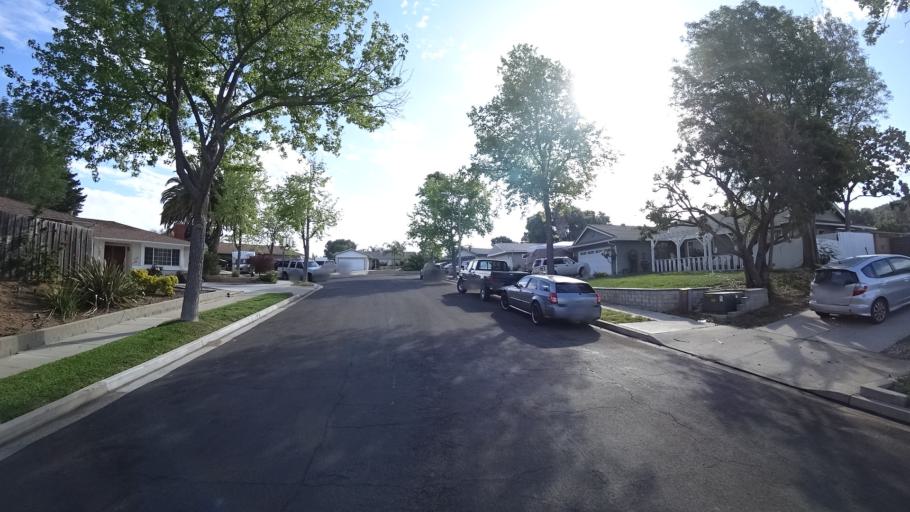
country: US
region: California
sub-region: Ventura County
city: Casa Conejo
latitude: 34.1722
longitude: -118.9532
